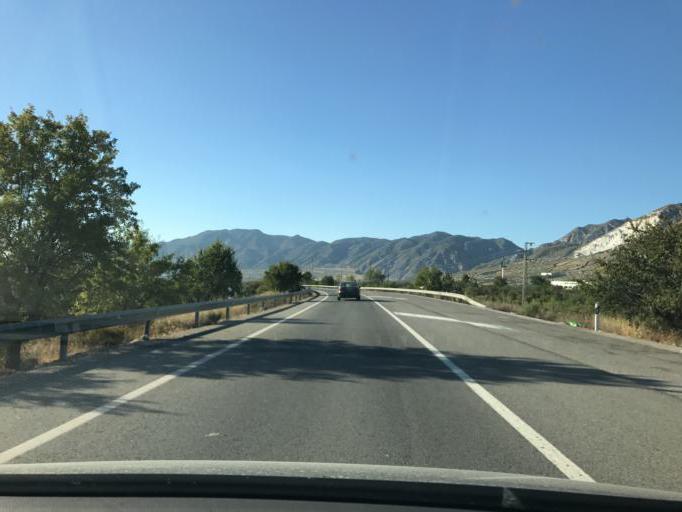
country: ES
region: Andalusia
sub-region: Provincia de Granada
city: Niguelas
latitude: 36.9696
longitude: -3.5575
